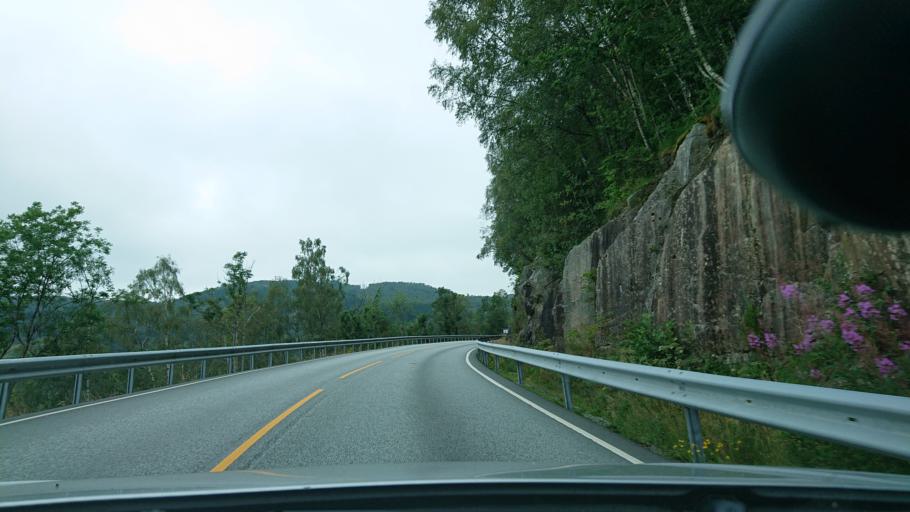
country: NO
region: Rogaland
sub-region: Hjelmeland
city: Hjelmelandsvagen
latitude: 59.1741
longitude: 6.1410
